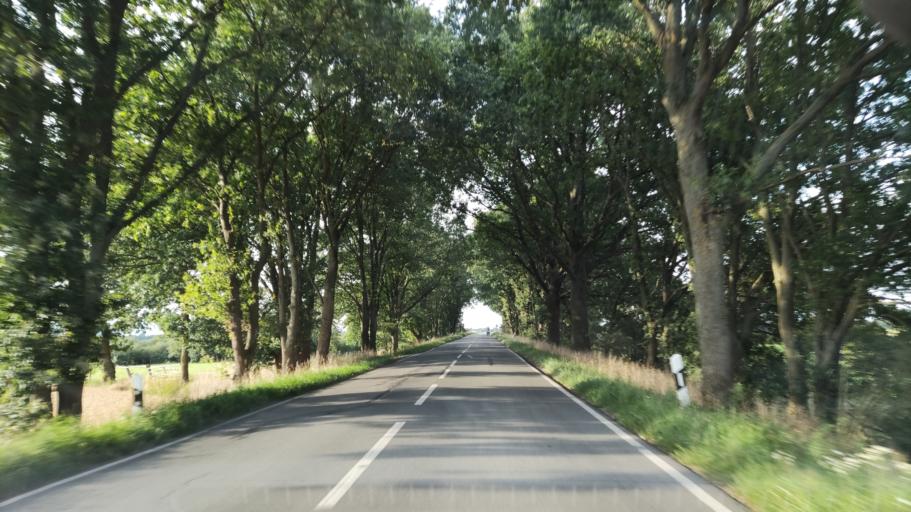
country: DE
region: Lower Saxony
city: Dannenberg
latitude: 53.1265
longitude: 11.1175
